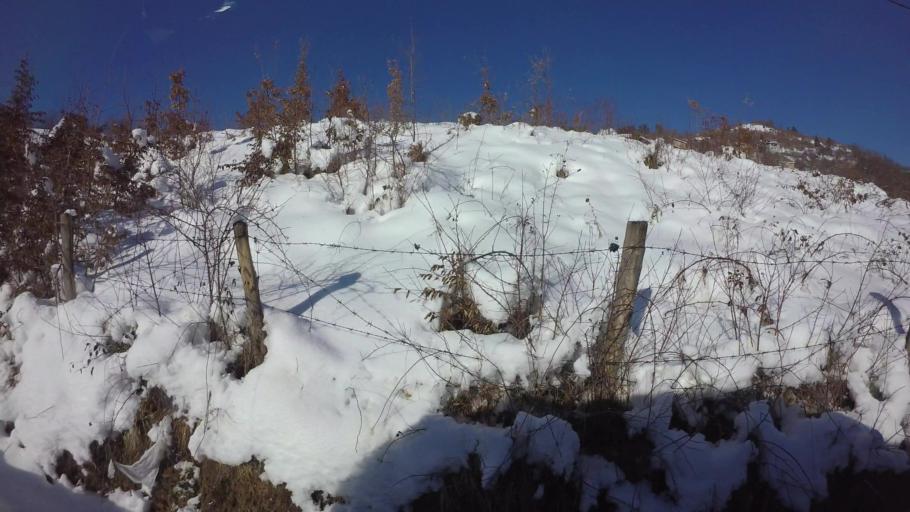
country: BA
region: Federation of Bosnia and Herzegovina
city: Kobilja Glava
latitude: 43.8947
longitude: 18.4095
